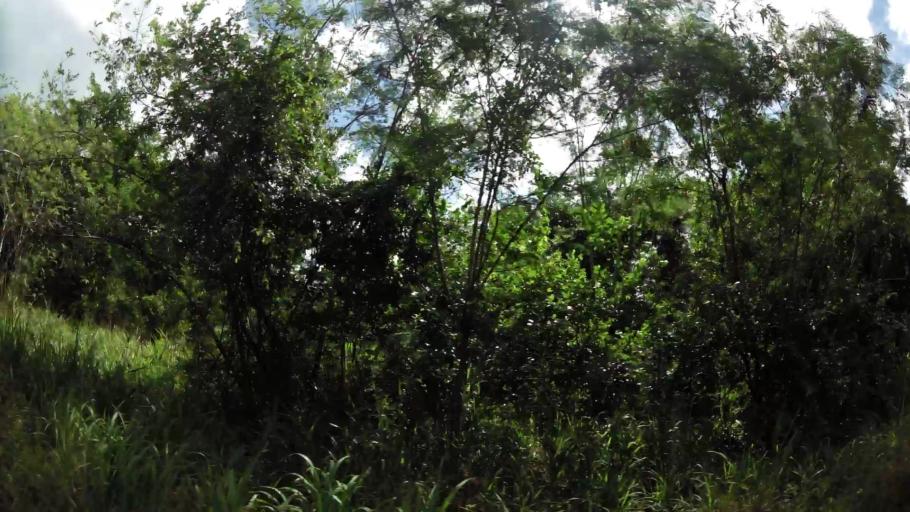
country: MQ
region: Martinique
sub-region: Martinique
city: Sainte-Luce
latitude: 14.4900
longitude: -60.9902
